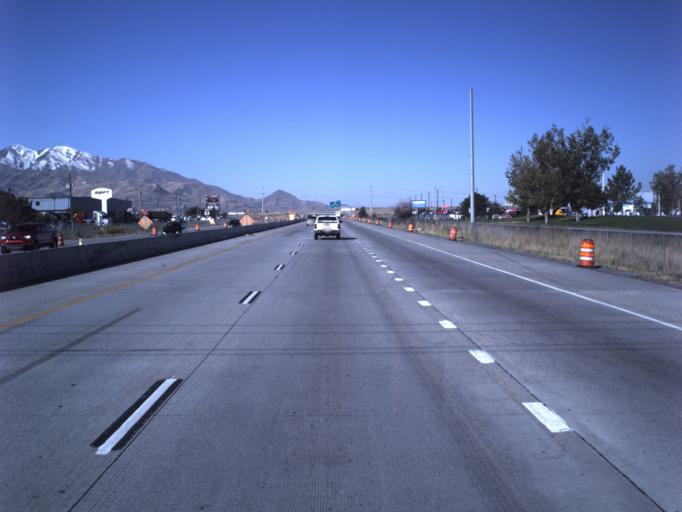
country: US
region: Utah
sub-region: Salt Lake County
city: West Valley City
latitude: 40.7259
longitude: -112.0121
